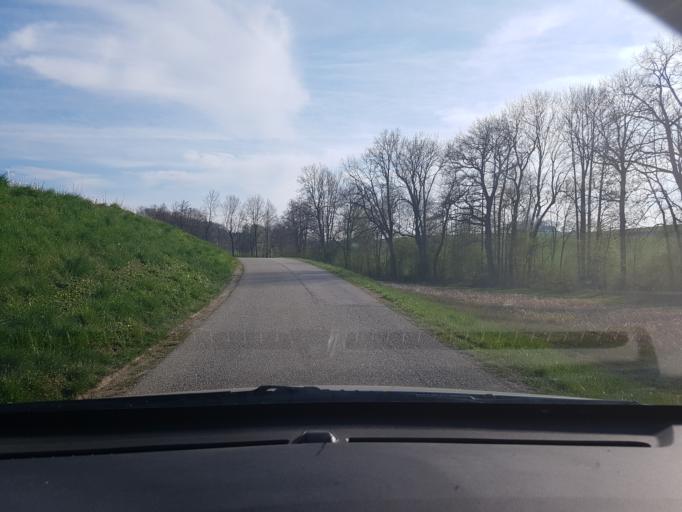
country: AT
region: Upper Austria
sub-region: Politischer Bezirk Linz-Land
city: Ansfelden
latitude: 48.1817
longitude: 14.3297
